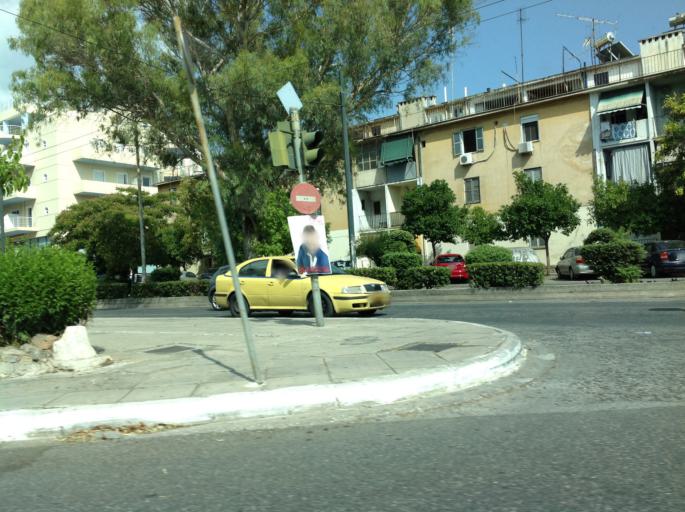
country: GR
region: Attica
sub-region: Nomarchia Athinas
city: Vyronas
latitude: 37.9702
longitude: 23.7544
